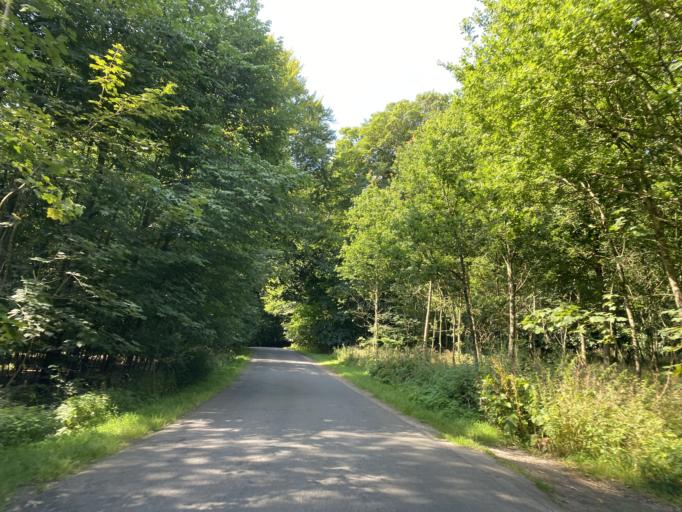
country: DK
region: Central Jutland
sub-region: Favrskov Kommune
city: Hammel
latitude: 56.2525
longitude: 9.8073
